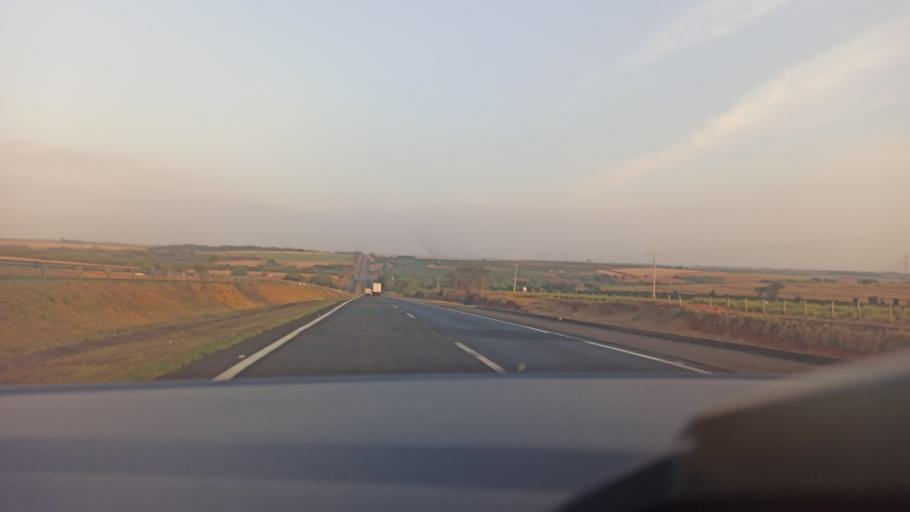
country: BR
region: Sao Paulo
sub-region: Santa Adelia
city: Santa Adelia
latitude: -21.3887
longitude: -48.7241
